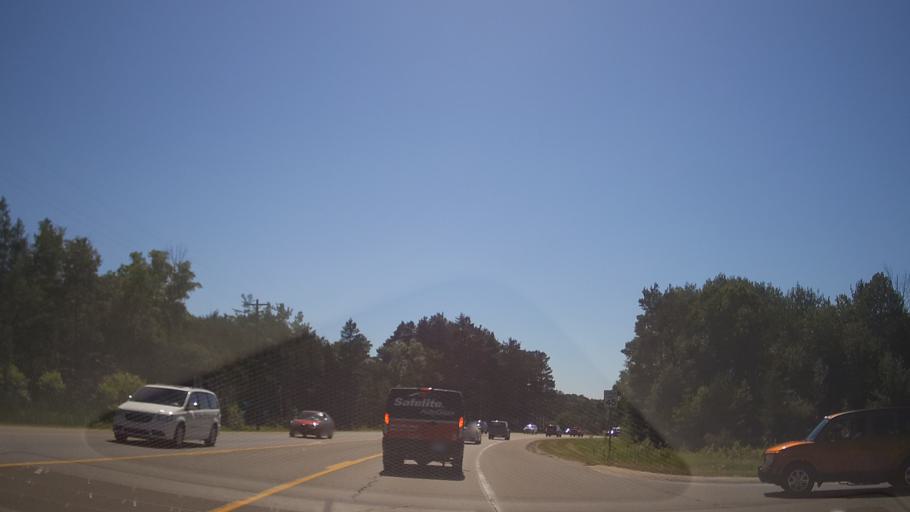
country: US
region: Michigan
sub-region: Emmet County
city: Petoskey
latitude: 45.3896
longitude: -84.9064
